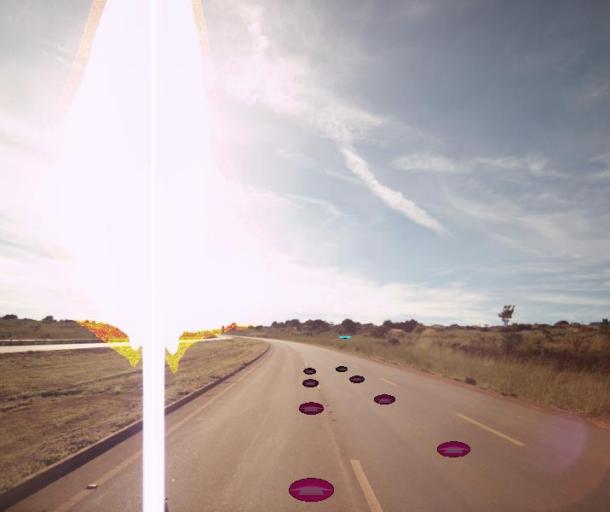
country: BR
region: Federal District
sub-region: Brasilia
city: Brasilia
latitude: -15.7560
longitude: -48.3342
